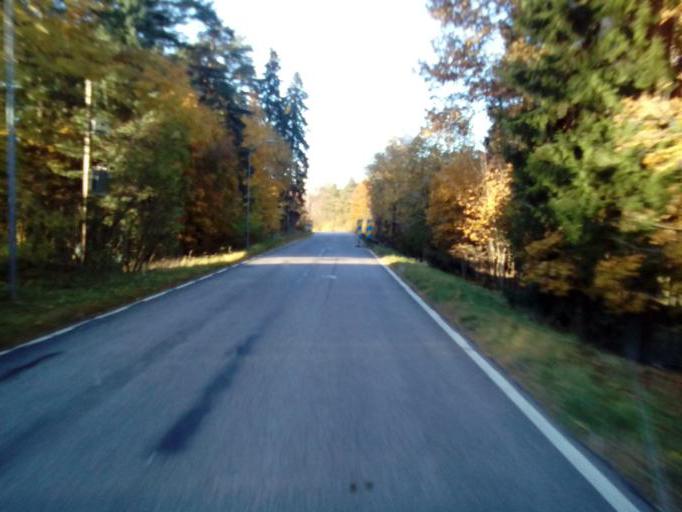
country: SE
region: OErebro
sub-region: Hallsbergs Kommun
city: Palsboda
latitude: 59.0212
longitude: 15.3787
